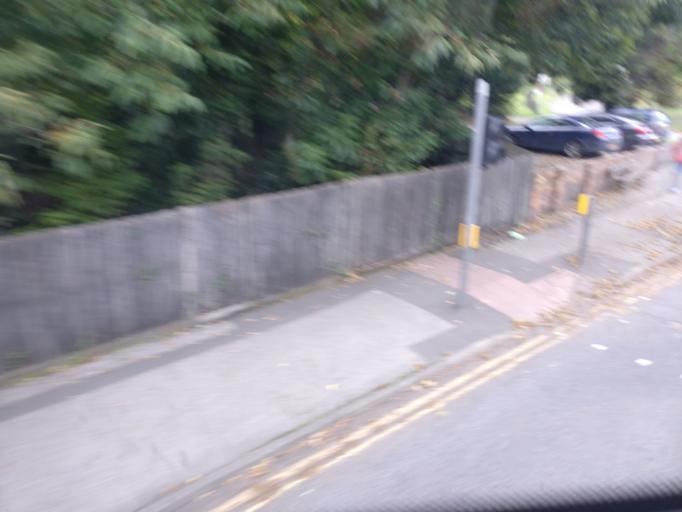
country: GB
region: England
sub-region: Surrey
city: Camberley
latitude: 51.3361
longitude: -0.7610
